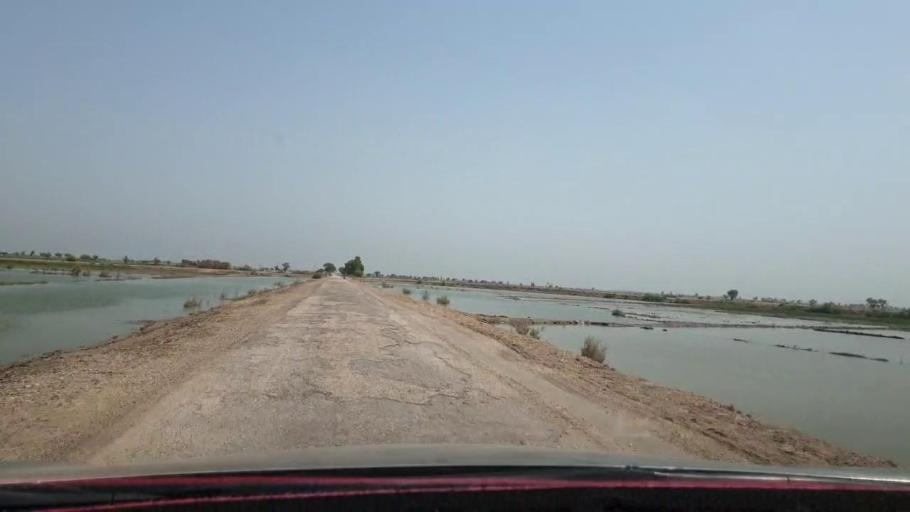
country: PK
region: Sindh
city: Warah
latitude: 27.3841
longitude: 67.7831
